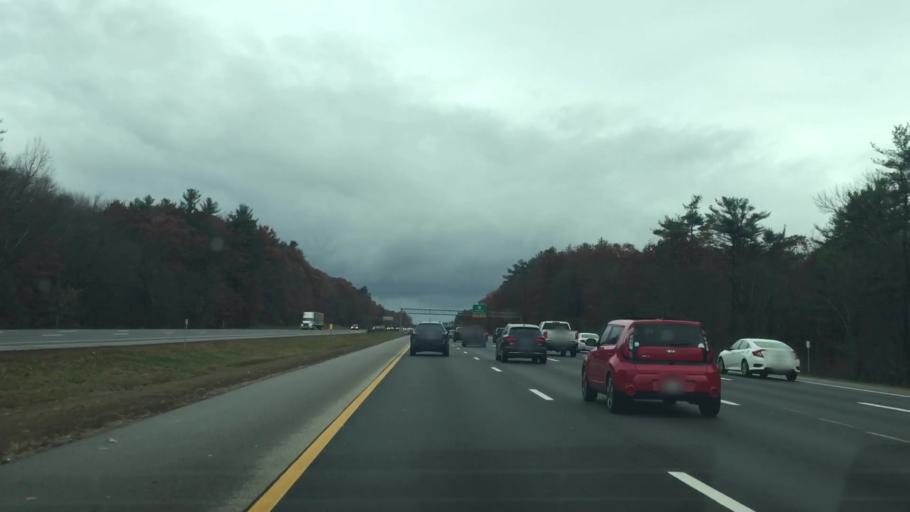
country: US
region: New Hampshire
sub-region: Rockingham County
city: Hampton
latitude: 42.9428
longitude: -70.8602
